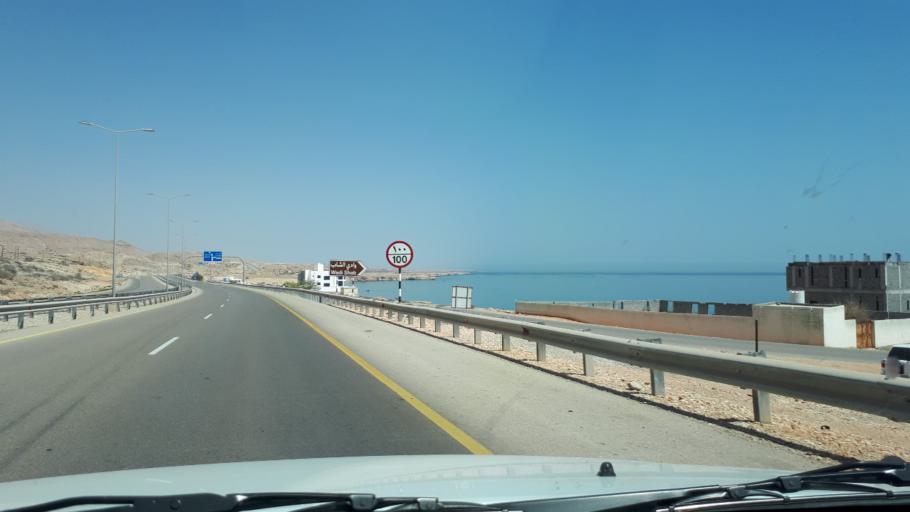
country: OM
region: Ash Sharqiyah
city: Sur
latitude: 22.8403
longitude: 59.2450
